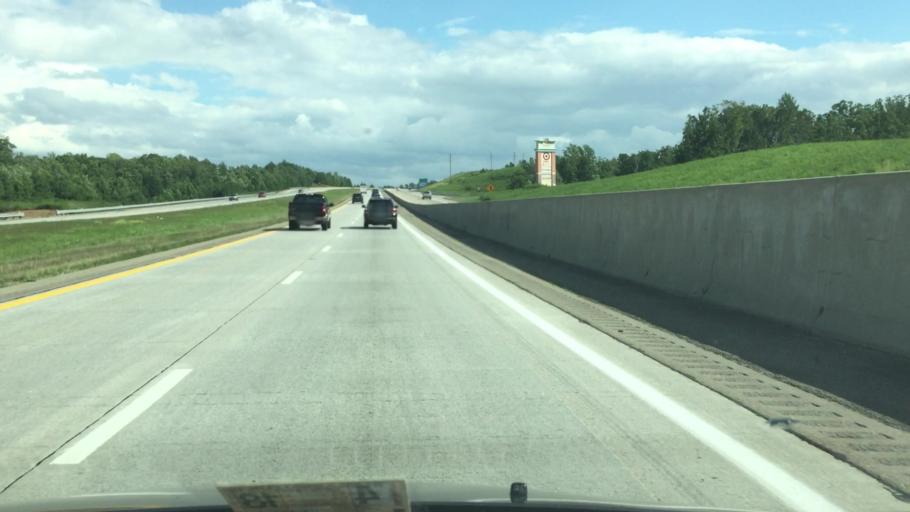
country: US
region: Virginia
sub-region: Chesterfield County
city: Brandermill
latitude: 37.5219
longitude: -77.6926
